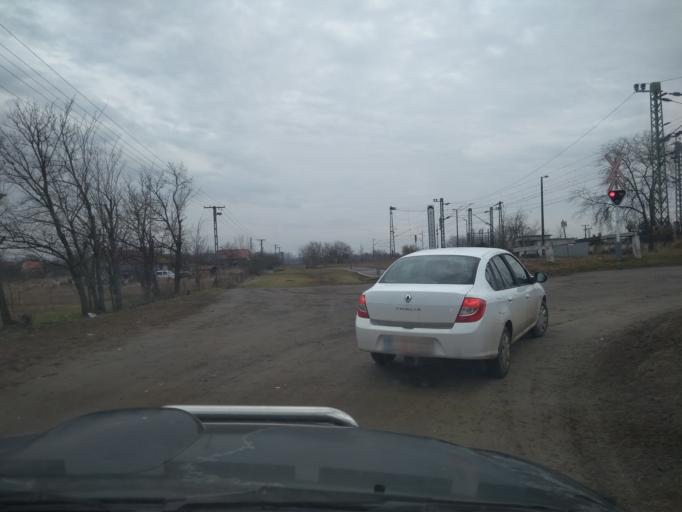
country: HU
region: Szabolcs-Szatmar-Bereg
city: Nyiregyhaza
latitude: 47.9672
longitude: 21.6853
